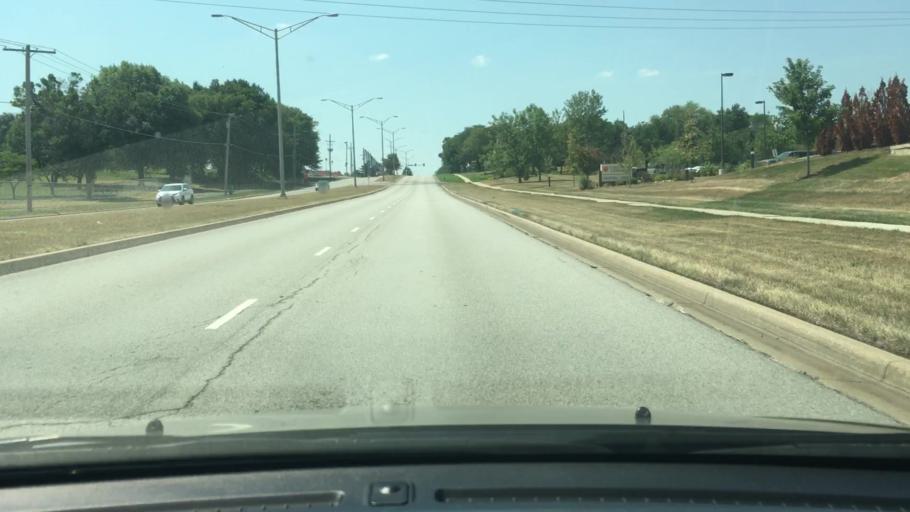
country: US
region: Kansas
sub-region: Johnson County
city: Lenexa
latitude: 38.9051
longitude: -94.7238
